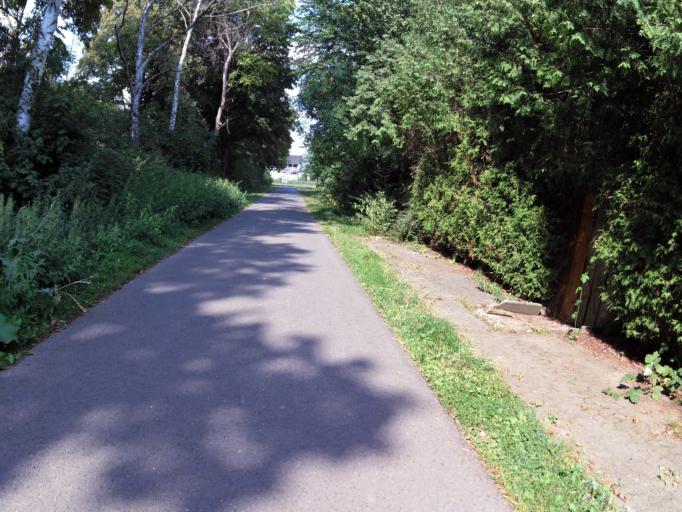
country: DE
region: North Rhine-Westphalia
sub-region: Regierungsbezirk Detmold
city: Minden
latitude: 52.2992
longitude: 8.9275
